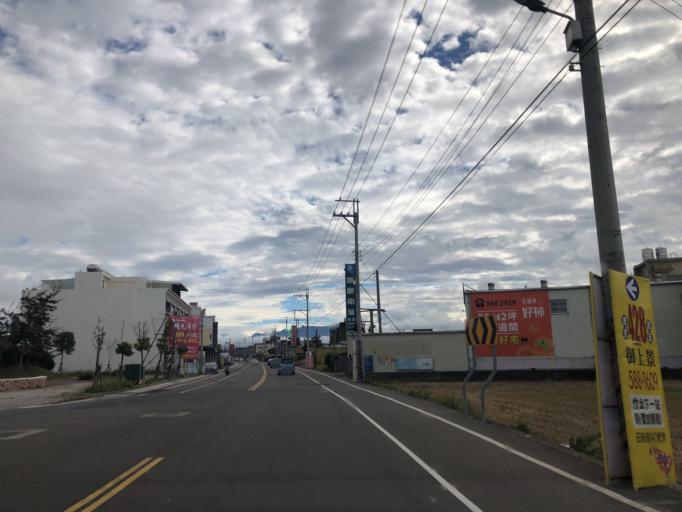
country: TW
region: Taiwan
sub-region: Hsinchu
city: Zhubei
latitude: 24.8263
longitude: 121.0702
